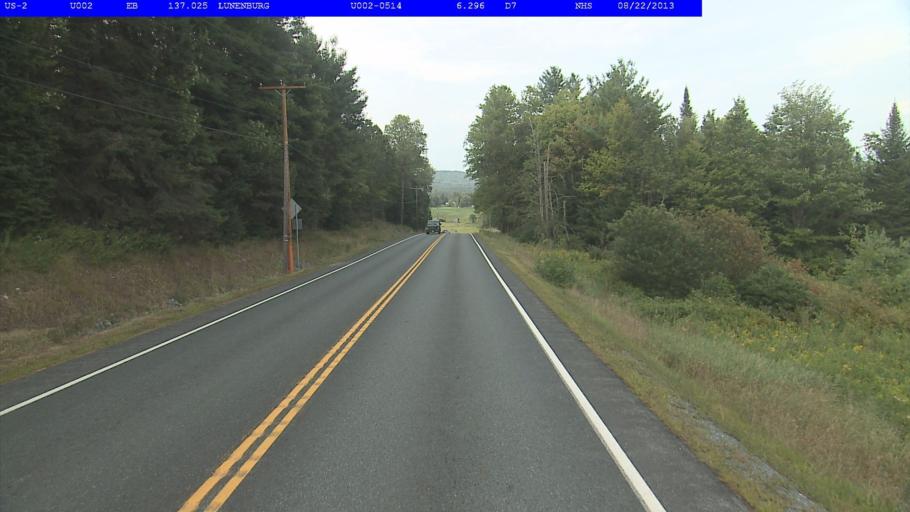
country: US
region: New Hampshire
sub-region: Coos County
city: Lancaster
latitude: 44.4669
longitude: -71.6517
